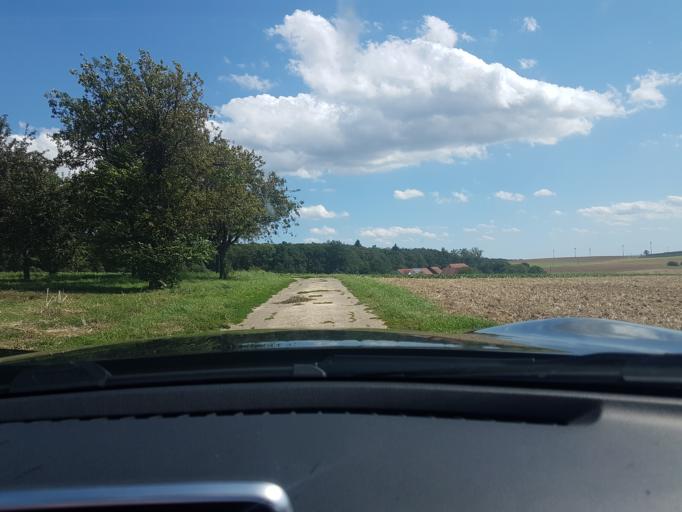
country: DE
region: Baden-Wuerttemberg
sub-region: Regierungsbezirk Stuttgart
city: Widdern
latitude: 49.3410
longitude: 9.3964
